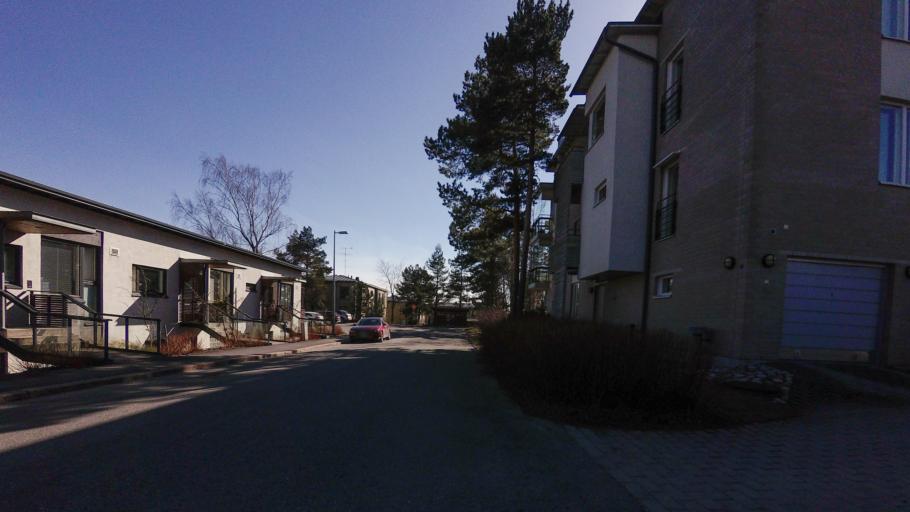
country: FI
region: Uusimaa
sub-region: Helsinki
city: Helsinki
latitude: 60.1851
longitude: 25.0132
